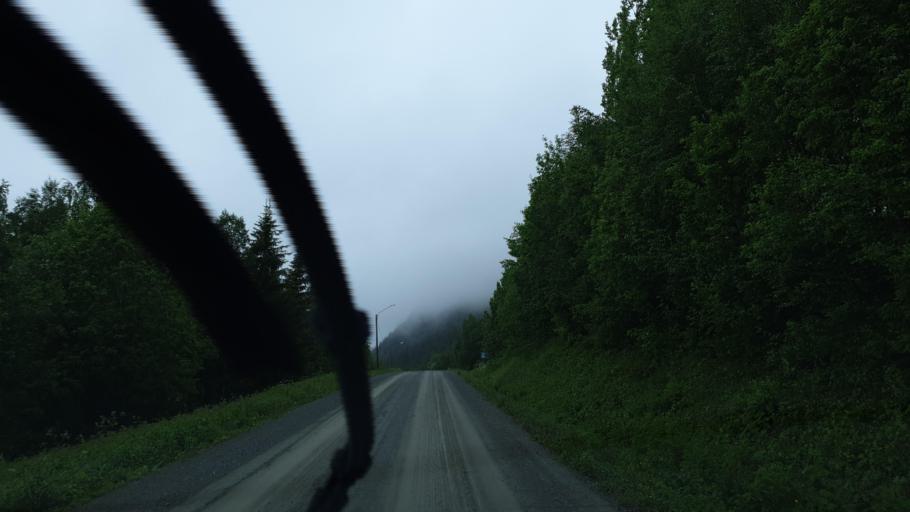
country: SE
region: Vaesterbotten
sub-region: Vilhelmina Kommun
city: Sjoberg
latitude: 65.3443
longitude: 15.8672
